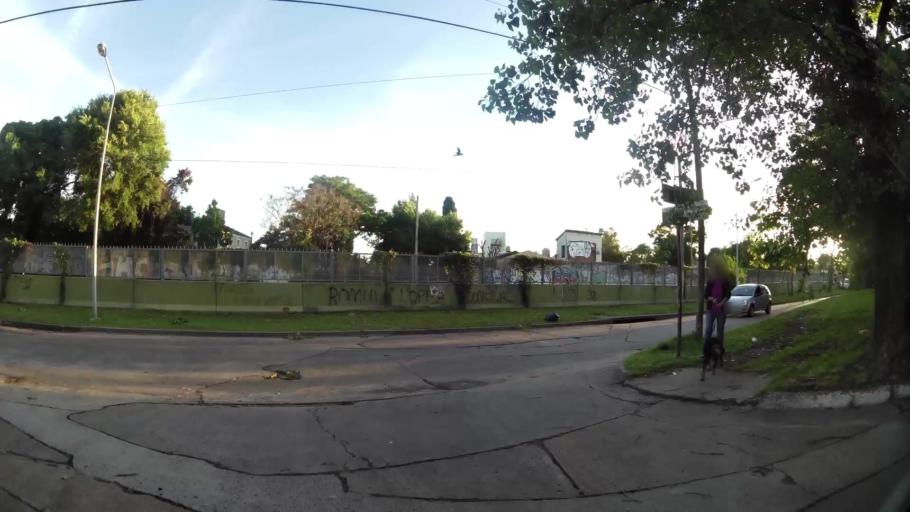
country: AR
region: Buenos Aires
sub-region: Partido de Moron
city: Moron
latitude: -34.6491
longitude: -58.6310
